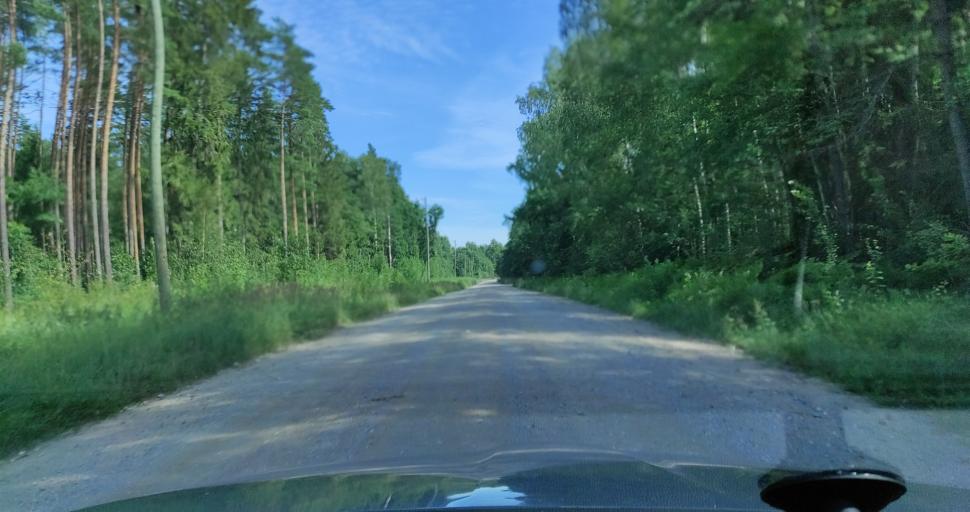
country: LV
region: Durbe
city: Liegi
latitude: 56.7534
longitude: 21.3504
